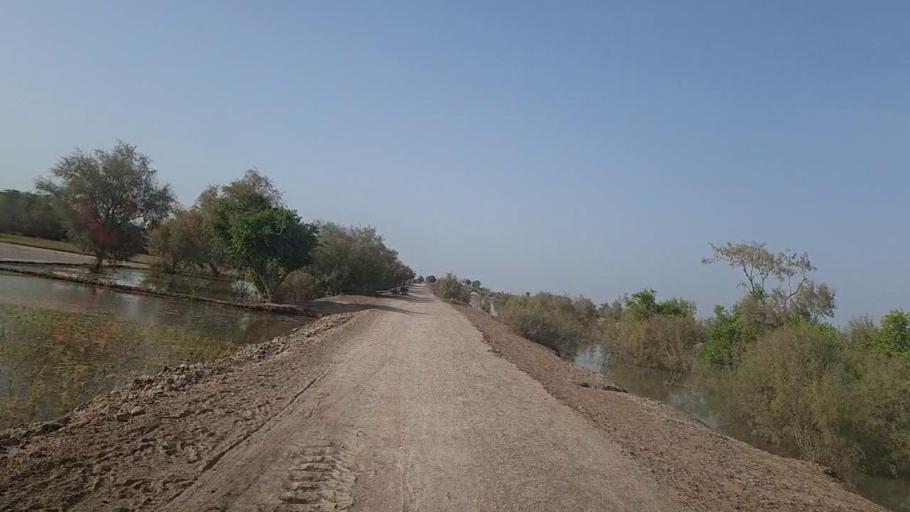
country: PK
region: Sindh
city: Sita Road
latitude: 27.1008
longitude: 67.8737
